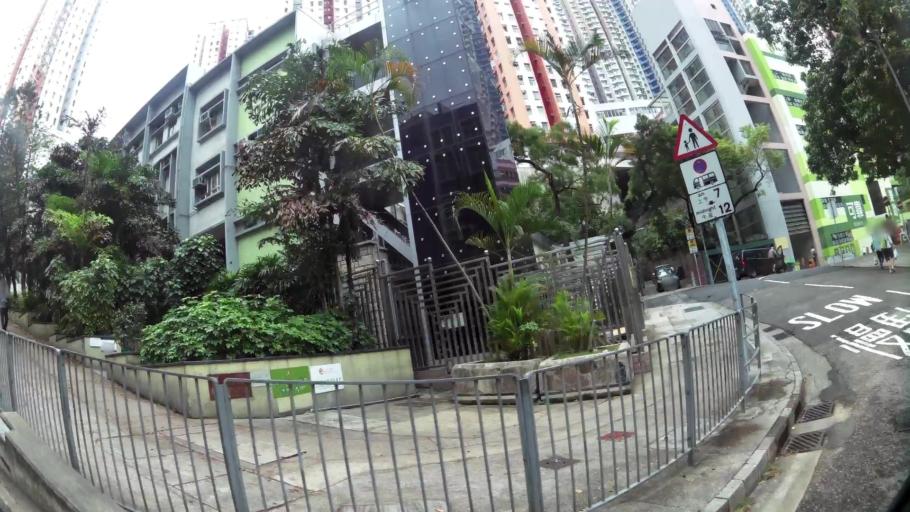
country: HK
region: Central and Western
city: Central
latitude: 22.2497
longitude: 114.1561
